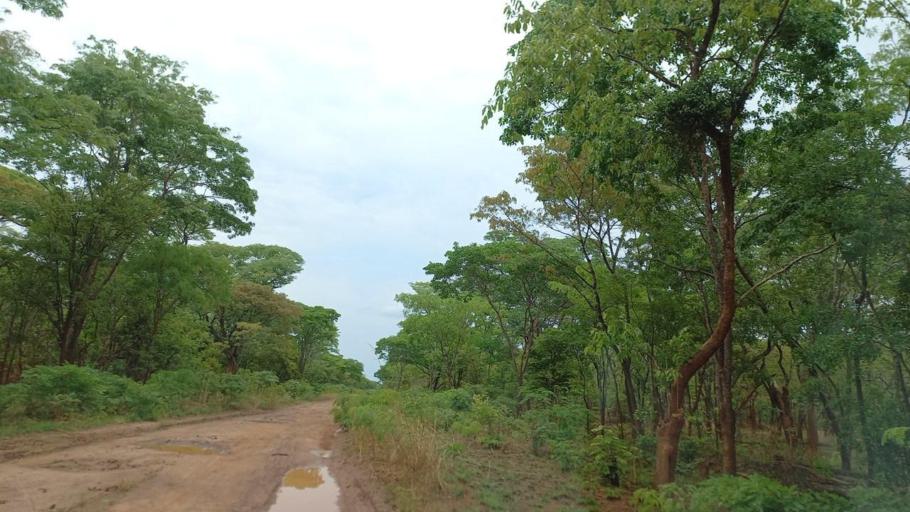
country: ZM
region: North-Western
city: Kalengwa
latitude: -13.6009
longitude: 24.9742
